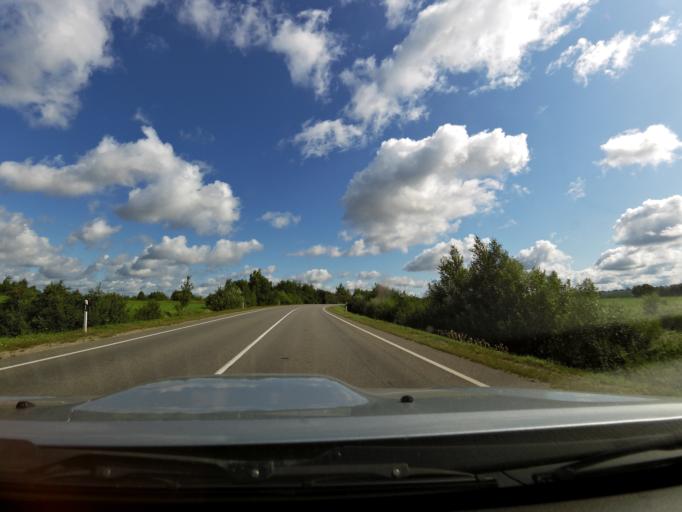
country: LT
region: Utenos apskritis
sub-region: Utena
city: Utena
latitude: 55.4860
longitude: 25.6440
